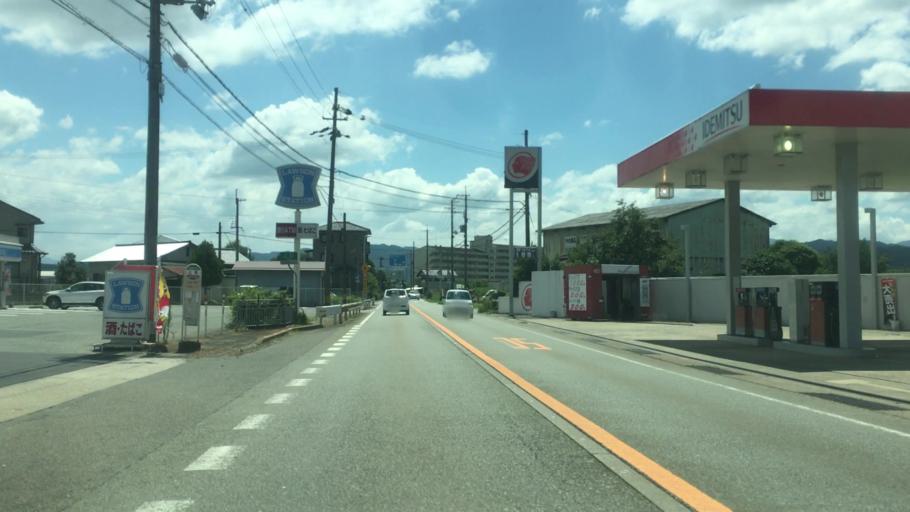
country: JP
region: Hyogo
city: Toyooka
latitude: 35.4975
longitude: 134.8036
